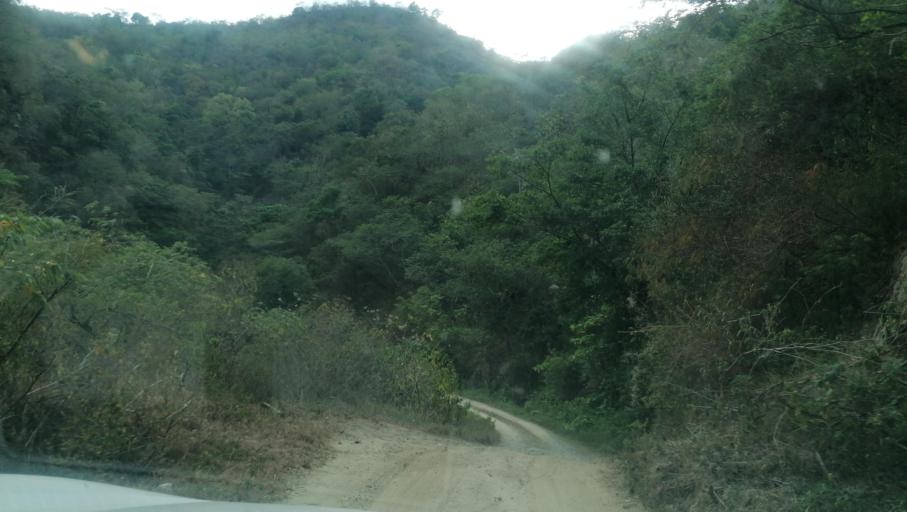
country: MX
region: Chiapas
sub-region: Cacahoatan
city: Benito Juarez
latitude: 15.1521
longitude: -92.1849
